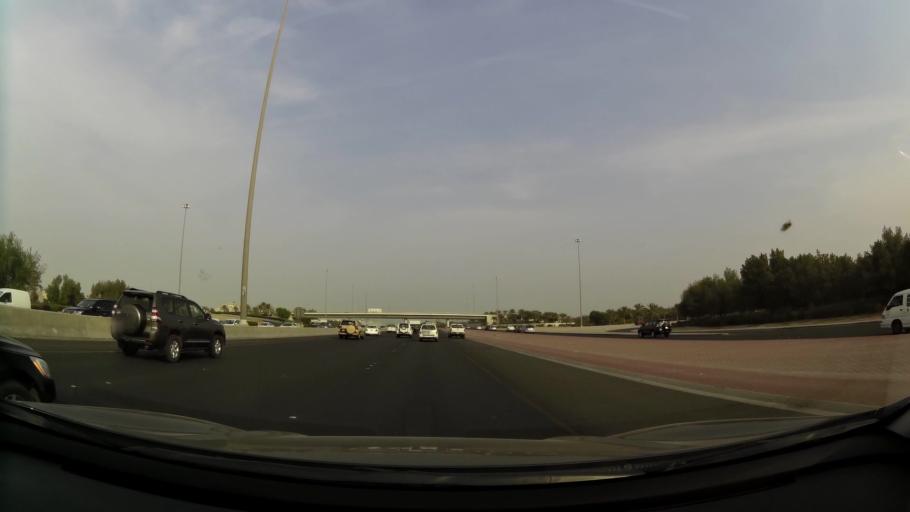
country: KW
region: Mubarak al Kabir
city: Sabah as Salim
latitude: 29.2641
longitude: 48.0195
